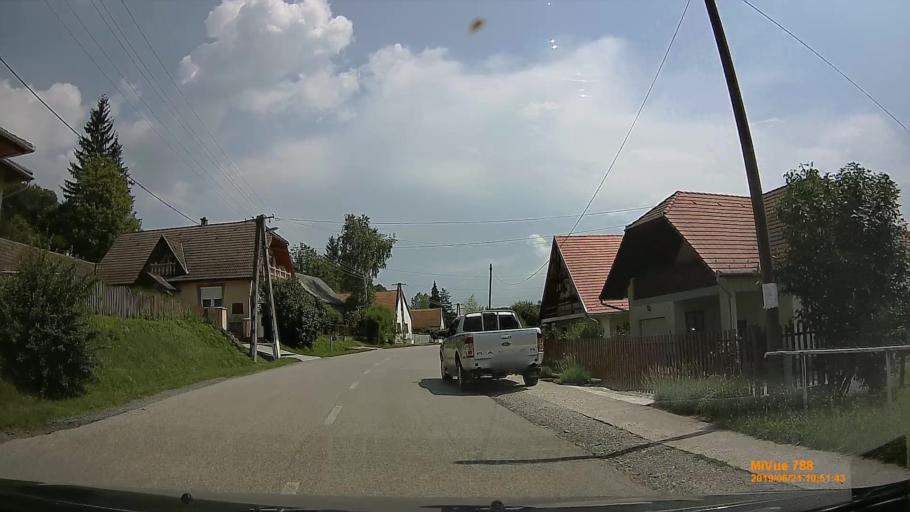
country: HU
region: Baranya
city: Buekkoesd
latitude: 46.1360
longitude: 18.0473
